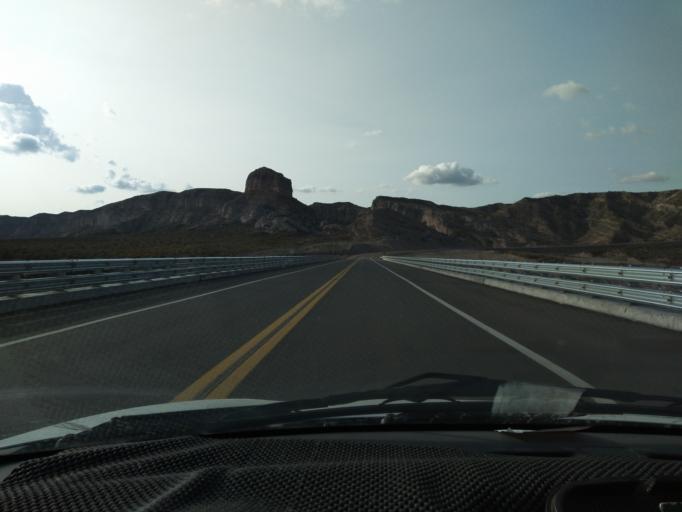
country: AR
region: Mendoza
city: San Rafael
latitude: -34.6393
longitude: -69.1801
